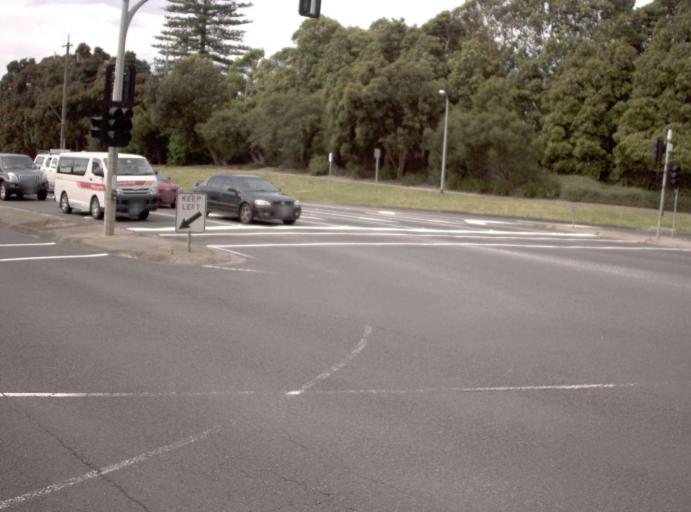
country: AU
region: Victoria
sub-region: Frankston
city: Frankston South
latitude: -38.1536
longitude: 145.1336
